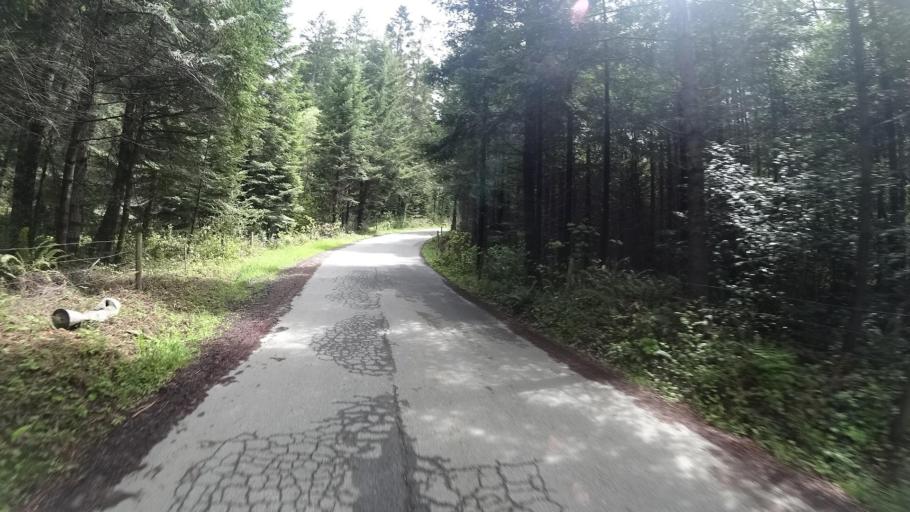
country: US
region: California
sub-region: Humboldt County
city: Blue Lake
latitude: 40.9048
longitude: -123.9833
